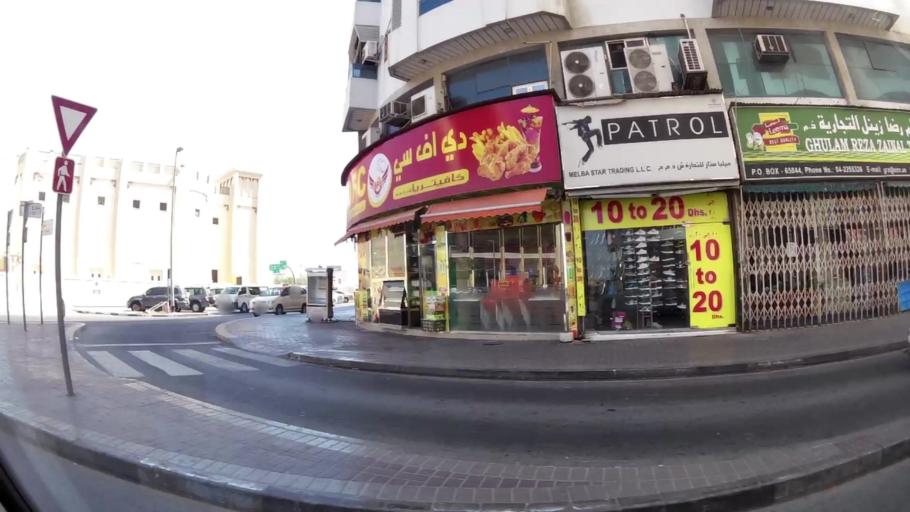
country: AE
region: Ash Shariqah
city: Sharjah
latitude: 25.2731
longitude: 55.2993
